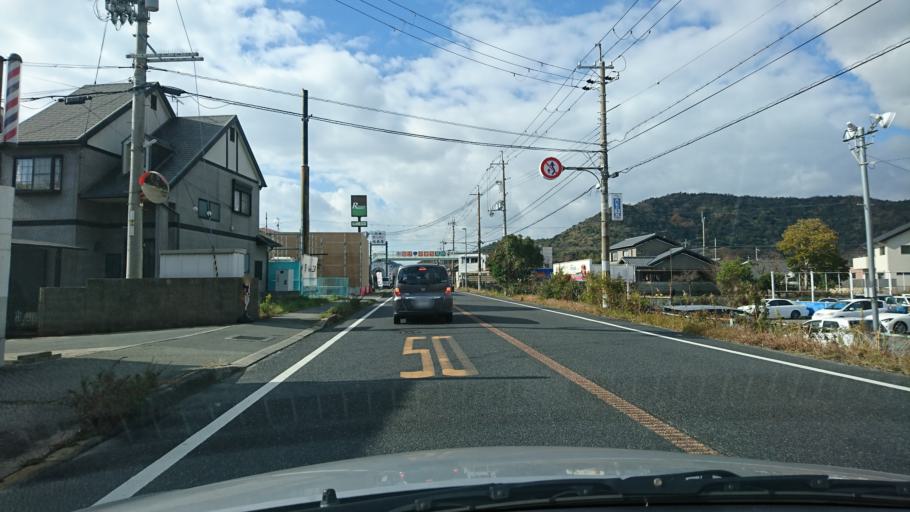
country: JP
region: Hyogo
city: Kakogawacho-honmachi
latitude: 34.7951
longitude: 134.7825
